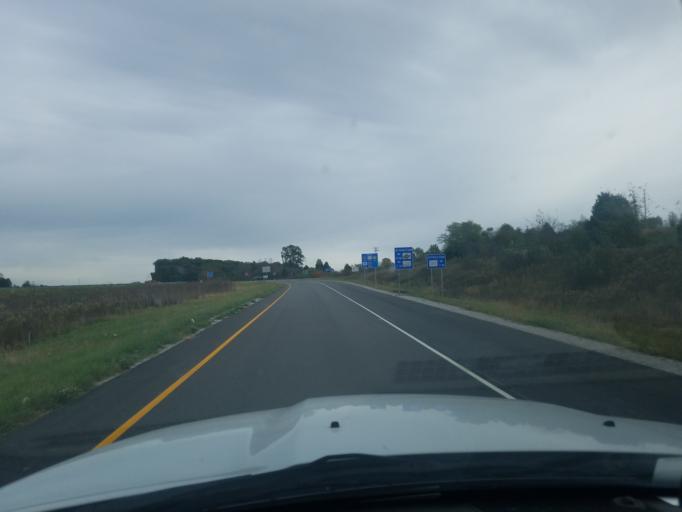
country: US
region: Indiana
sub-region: Dubois County
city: Ferdinand
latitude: 38.2052
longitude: -86.8679
